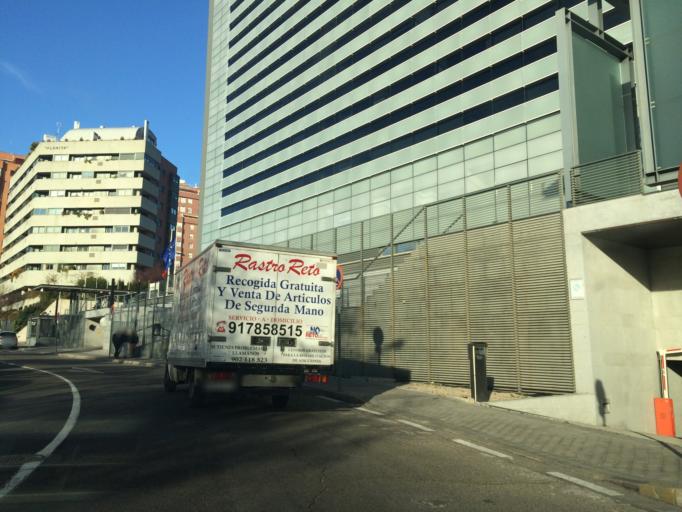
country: ES
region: Madrid
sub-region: Provincia de Madrid
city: Pinar de Chamartin
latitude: 40.4736
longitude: -3.6721
